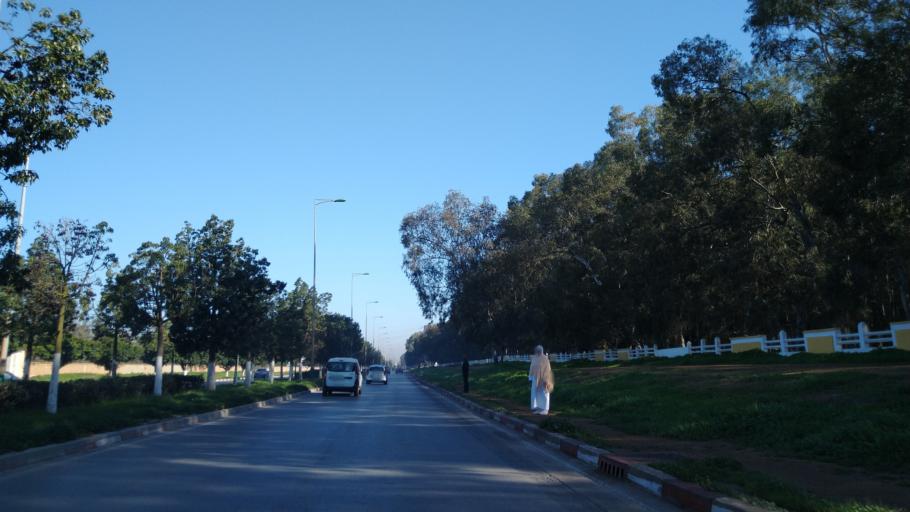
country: MA
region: Rabat-Sale-Zemmour-Zaer
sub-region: Skhirate-Temara
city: Temara
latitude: 33.9308
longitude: -6.8894
